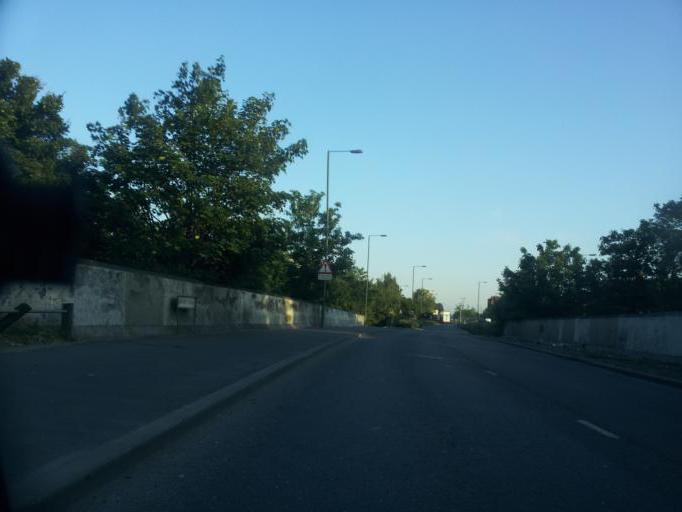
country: GB
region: England
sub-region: Greater London
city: Erith
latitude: 51.4761
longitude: 0.1817
